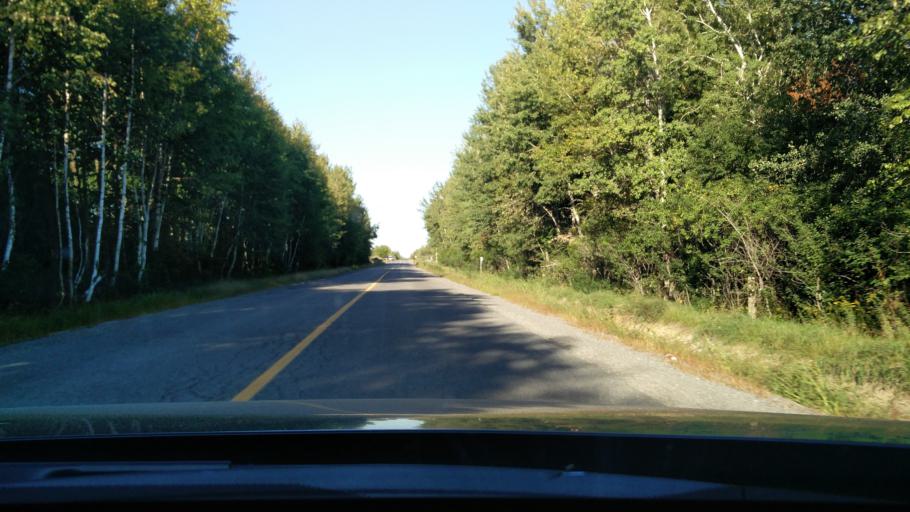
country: CA
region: Ontario
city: Bells Corners
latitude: 45.2201
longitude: -75.7648
